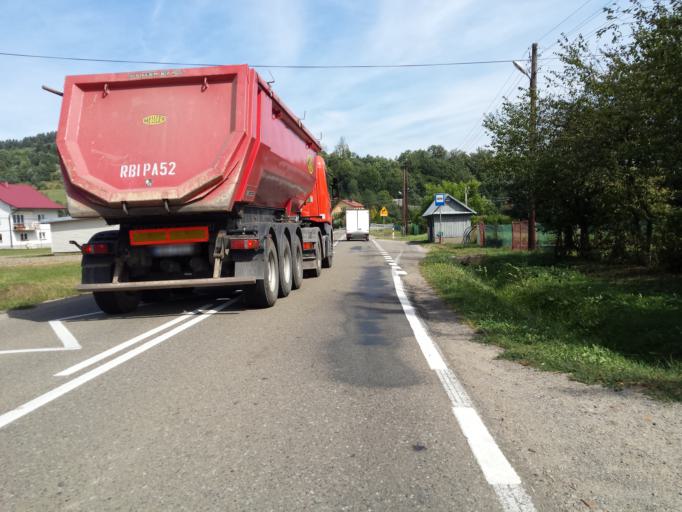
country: PL
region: Subcarpathian Voivodeship
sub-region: Powiat leski
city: Baligrod
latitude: 49.4040
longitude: 22.2895
